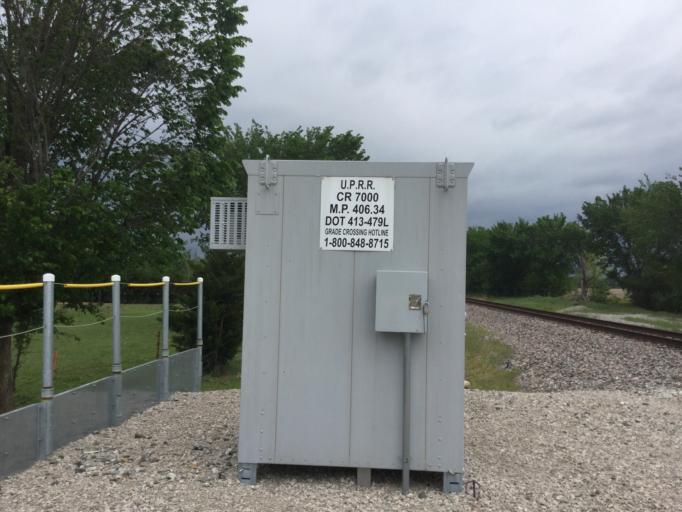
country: US
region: Kansas
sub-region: Labette County
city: Chetopa
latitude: 37.0915
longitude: -95.1141
